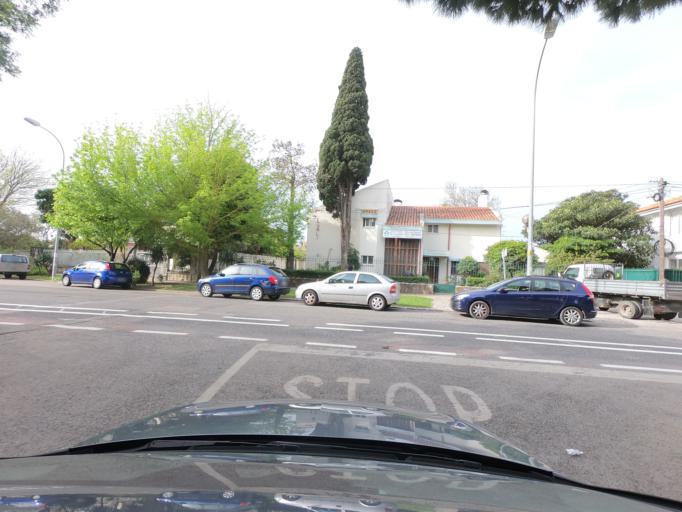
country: PT
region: Lisbon
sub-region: Oeiras
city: Carcavelos
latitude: 38.6902
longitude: -9.3224
